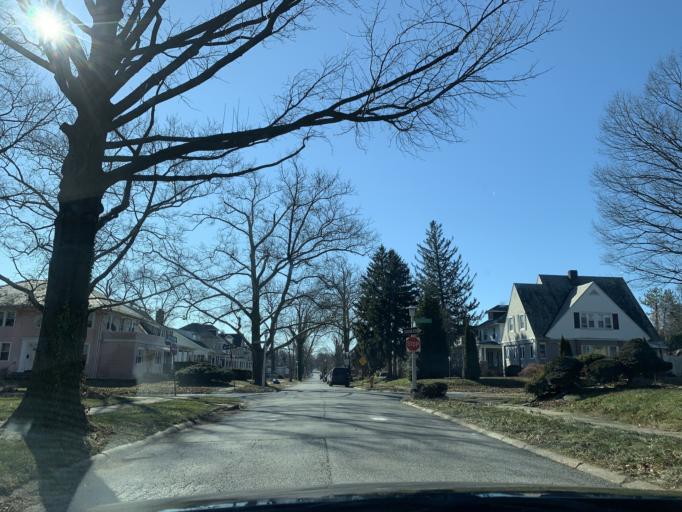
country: US
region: Maryland
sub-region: Baltimore County
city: Lochearn
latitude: 39.3278
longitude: -76.6754
